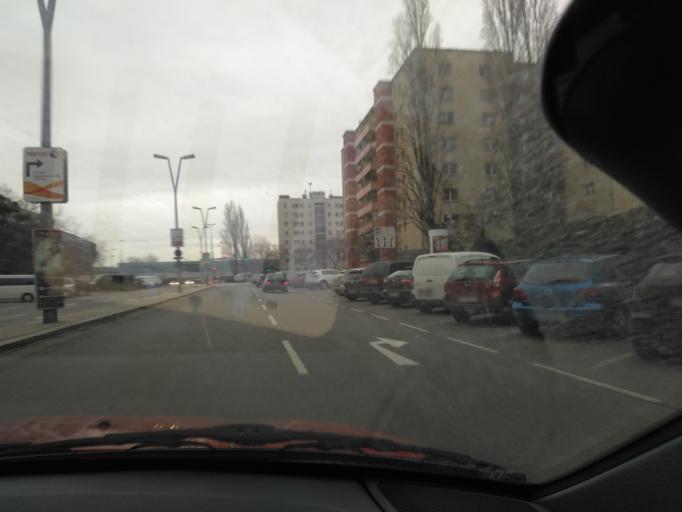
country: AT
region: Vienna
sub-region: Wien Stadt
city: Vienna
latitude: 48.2121
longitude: 16.4228
